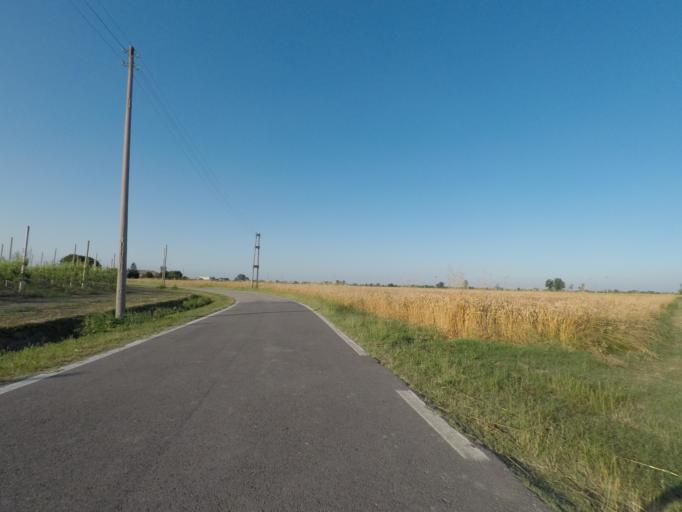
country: IT
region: Veneto
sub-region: Provincia di Rovigo
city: Villamarzana
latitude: 45.0287
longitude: 11.6766
